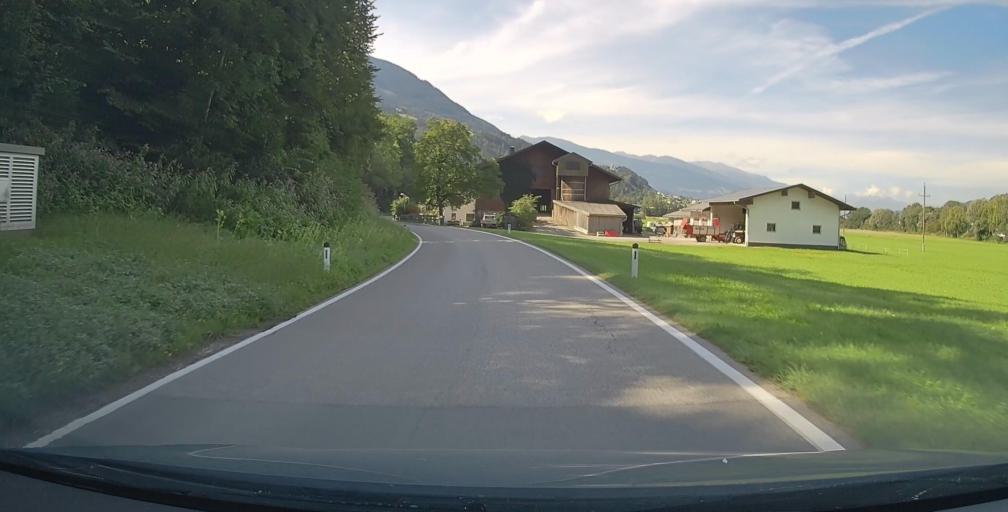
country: AT
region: Tyrol
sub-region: Politischer Bezirk Schwaz
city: Stans
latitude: 47.3619
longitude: 11.7364
